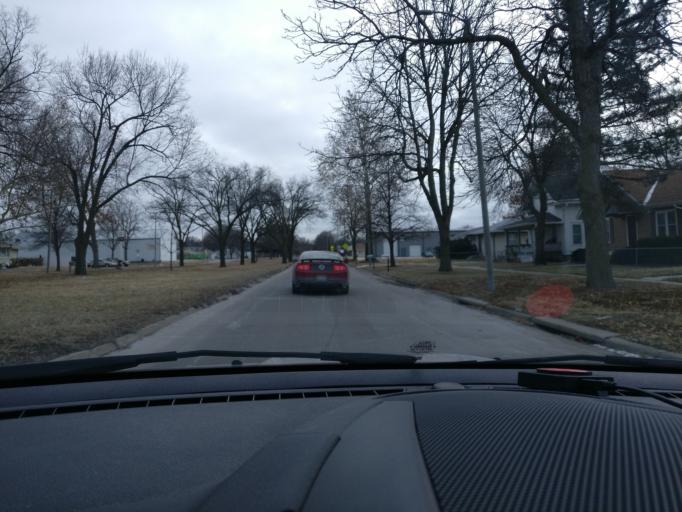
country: US
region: Nebraska
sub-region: Lancaster County
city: Lincoln
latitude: 40.8527
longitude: -96.6402
